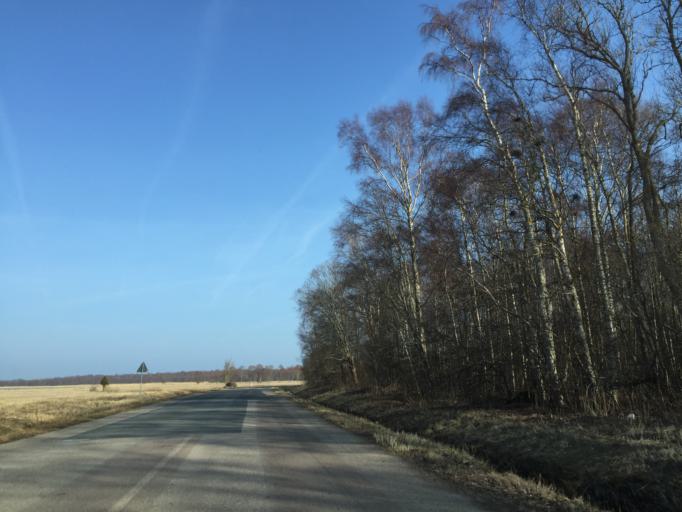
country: EE
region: Saare
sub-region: Kuressaare linn
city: Kuressaare
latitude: 58.0624
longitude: 22.1482
